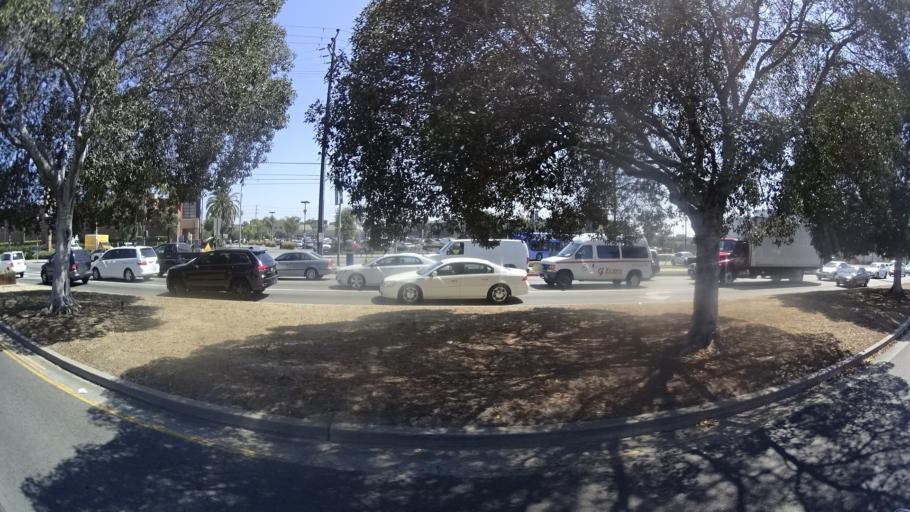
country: US
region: California
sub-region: Los Angeles County
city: West Hollywood
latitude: 34.0487
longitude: -118.3399
